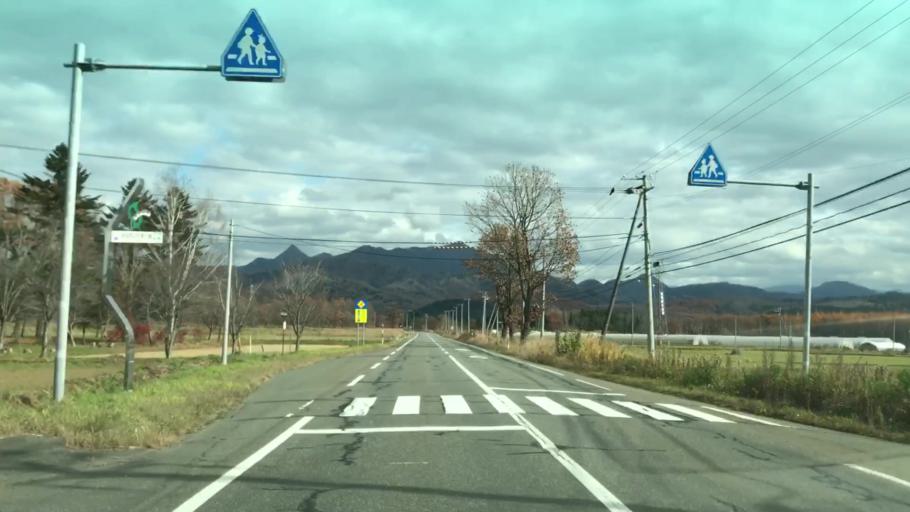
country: JP
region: Hokkaido
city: Shizunai-furukawacho
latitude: 42.7329
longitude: 142.3486
